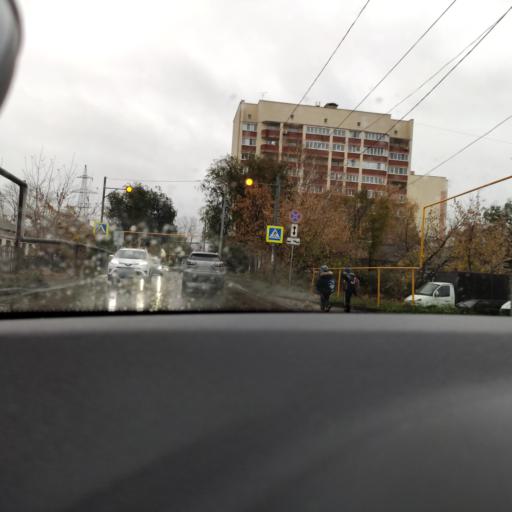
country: RU
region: Samara
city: Samara
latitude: 53.1574
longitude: 50.0872
